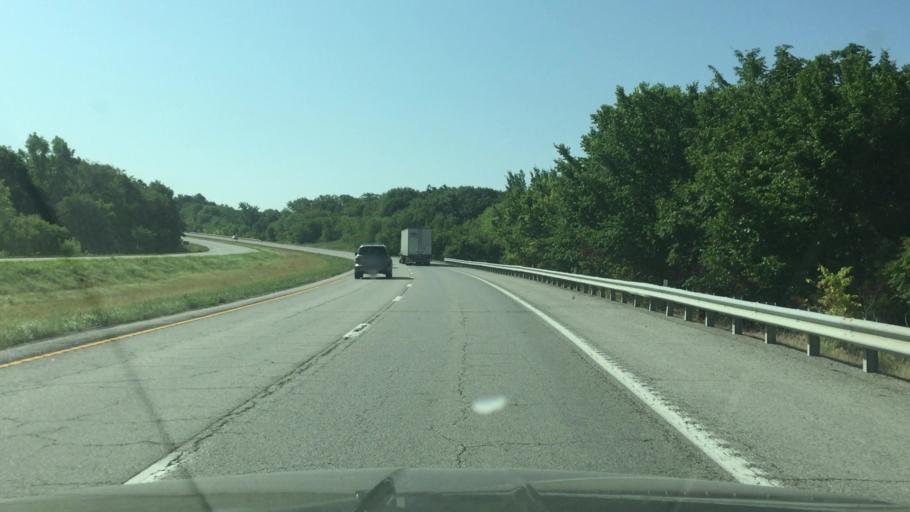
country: US
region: Missouri
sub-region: Johnson County
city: Warrensburg
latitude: 38.7846
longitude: -93.8642
